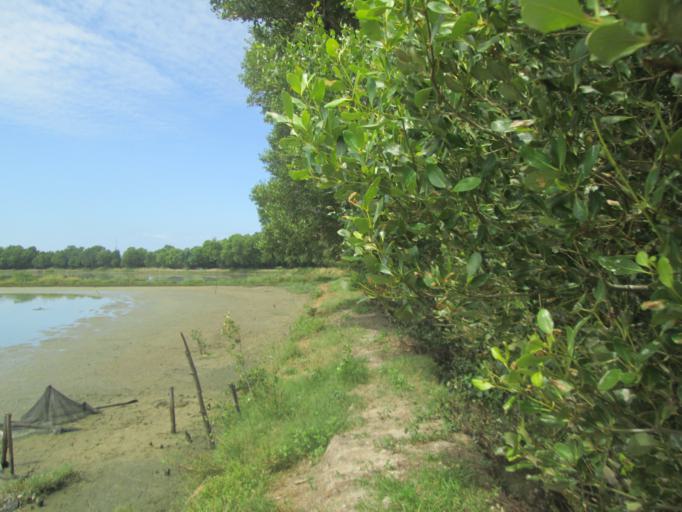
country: PH
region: Ilocos
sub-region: Province of Pangasinan
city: Pangapisan
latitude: 16.2471
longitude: 119.9268
